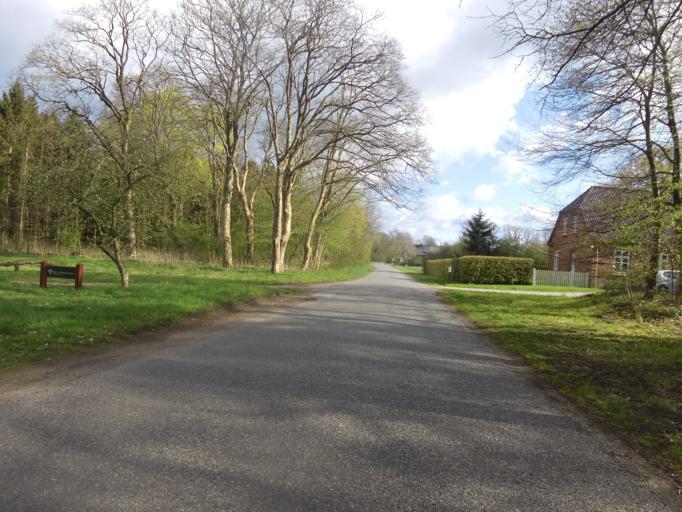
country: DK
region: South Denmark
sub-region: Haderslev Kommune
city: Gram
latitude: 55.2625
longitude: 8.9555
